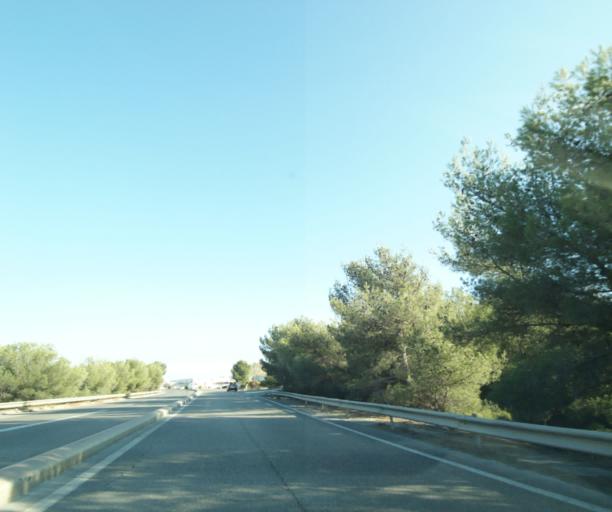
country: FR
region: Provence-Alpes-Cote d'Azur
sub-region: Departement des Bouches-du-Rhone
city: Chateauneuf-les-Martigues
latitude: 43.3946
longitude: 5.1298
